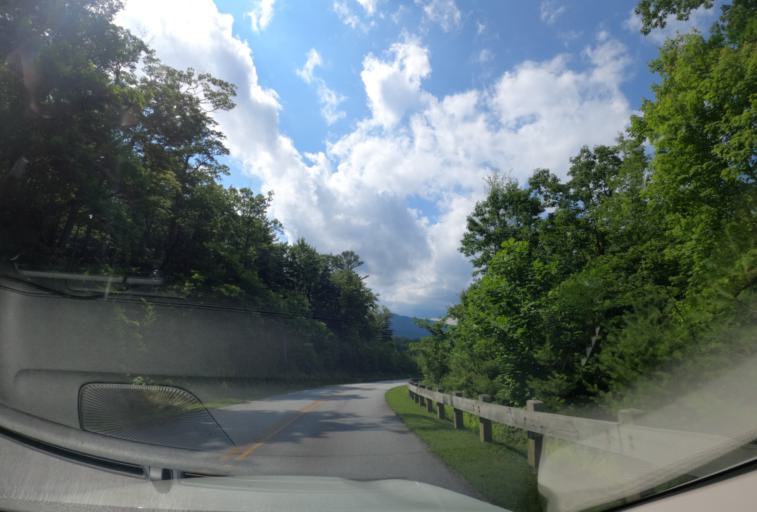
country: US
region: North Carolina
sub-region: Transylvania County
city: Brevard
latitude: 35.0985
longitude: -82.9518
